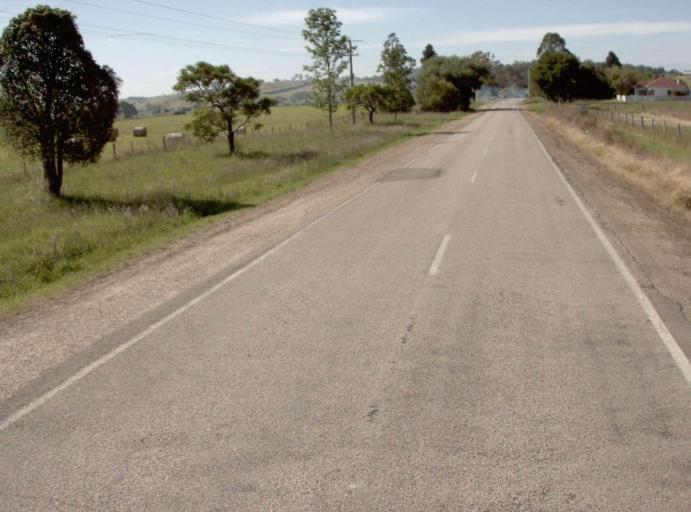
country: AU
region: Victoria
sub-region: East Gippsland
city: Bairnsdale
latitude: -37.7293
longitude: 147.8095
